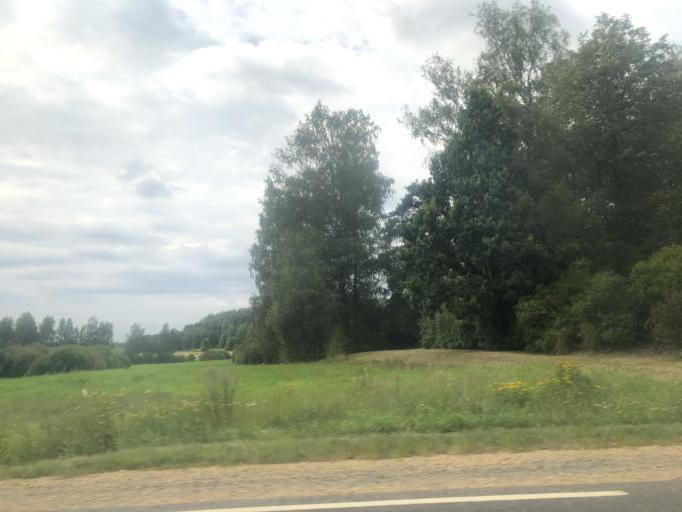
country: LV
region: Baldone
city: Baldone
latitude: 56.7181
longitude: 24.3724
